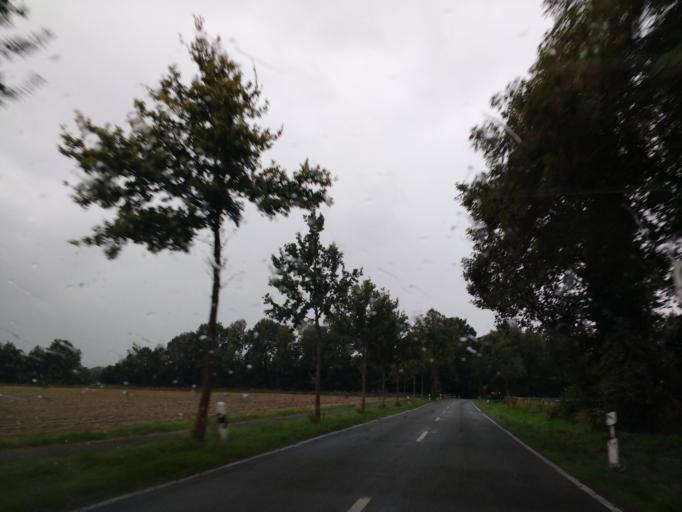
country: DE
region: North Rhine-Westphalia
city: Rietberg
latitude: 51.7400
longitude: 8.4452
